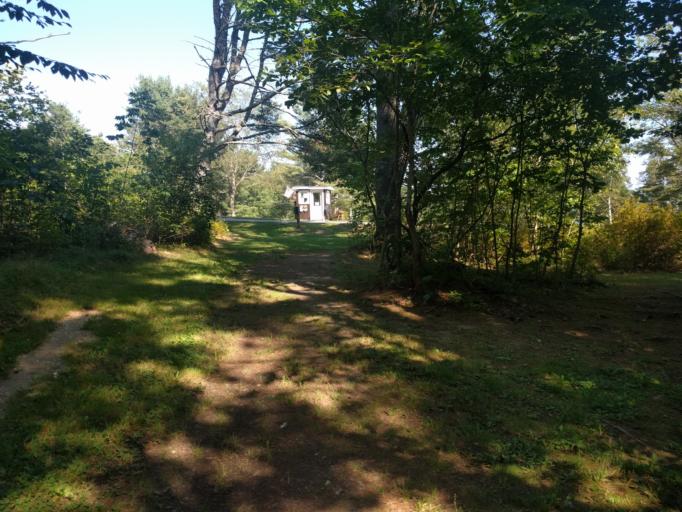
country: US
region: Maine
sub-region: Waldo County
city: Belfast
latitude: 44.4339
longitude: -68.9452
